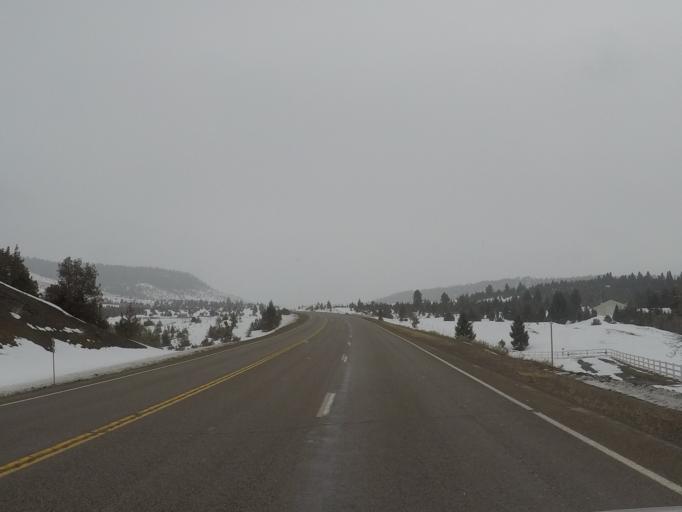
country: US
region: Montana
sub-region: Meagher County
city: White Sulphur Springs
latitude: 46.6689
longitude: -110.8776
